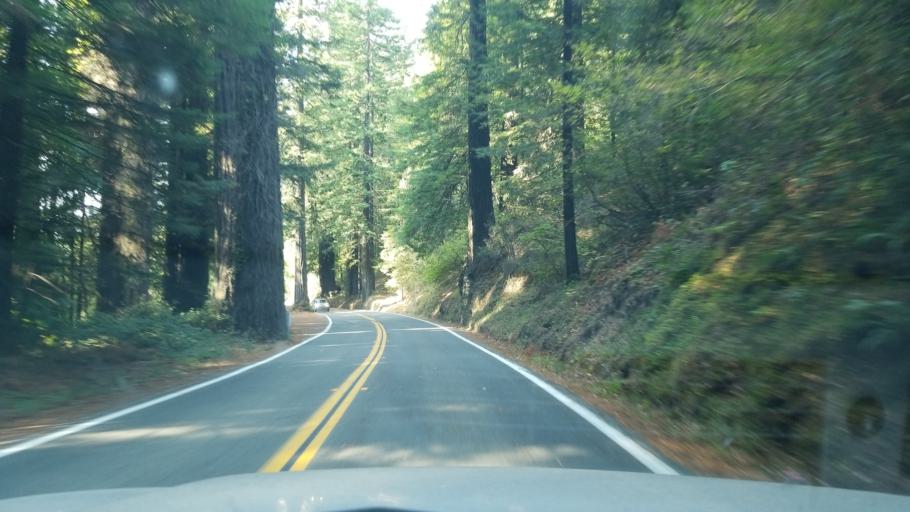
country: US
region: California
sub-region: Humboldt County
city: Redway
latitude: 40.2445
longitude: -123.8216
